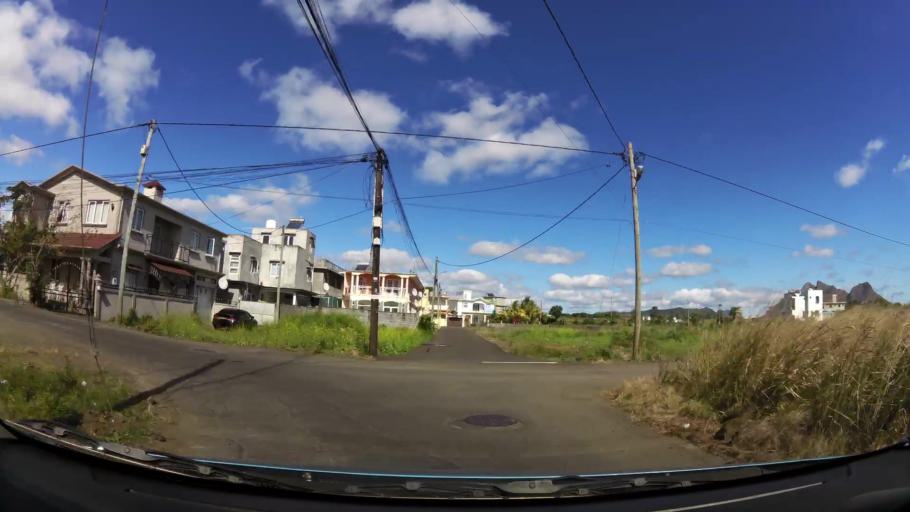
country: MU
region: Plaines Wilhems
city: Vacoas
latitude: -20.2827
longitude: 57.4738
